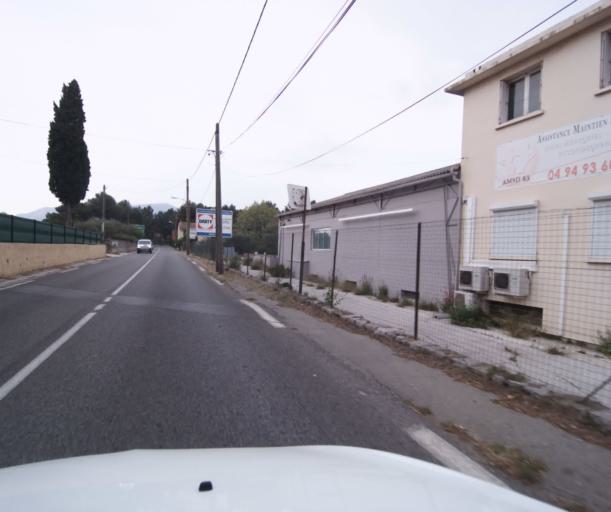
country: FR
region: Provence-Alpes-Cote d'Azur
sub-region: Departement du Var
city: La Garde
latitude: 43.1116
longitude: 5.9991
